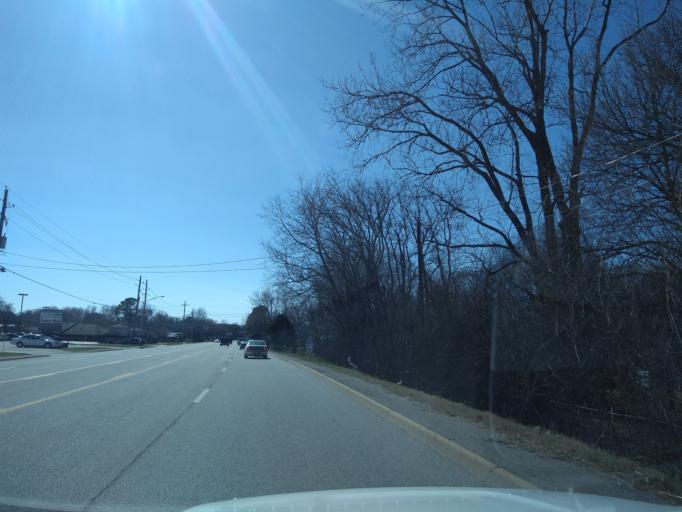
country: US
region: Arkansas
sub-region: Washington County
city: Farmington
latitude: 36.0451
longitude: -94.2303
